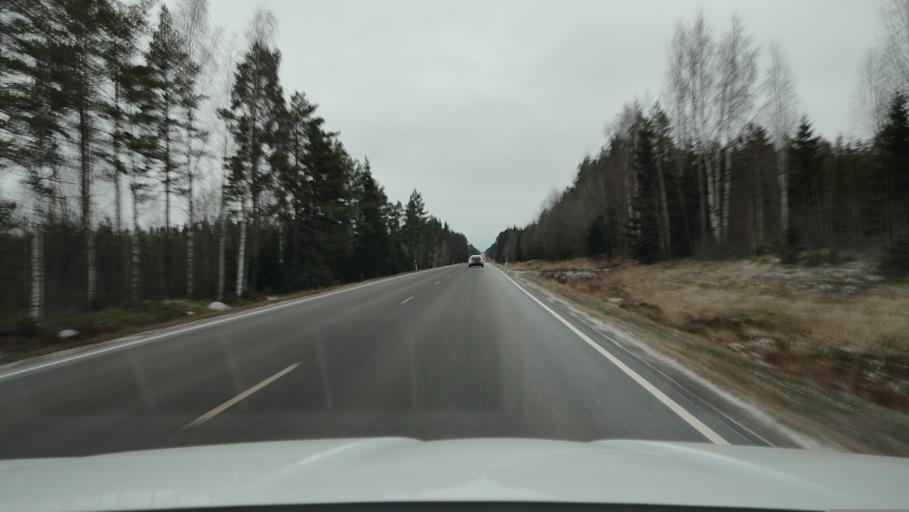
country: FI
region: Ostrobothnia
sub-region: Sydosterbotten
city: Naerpes
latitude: 62.5779
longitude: 21.4918
